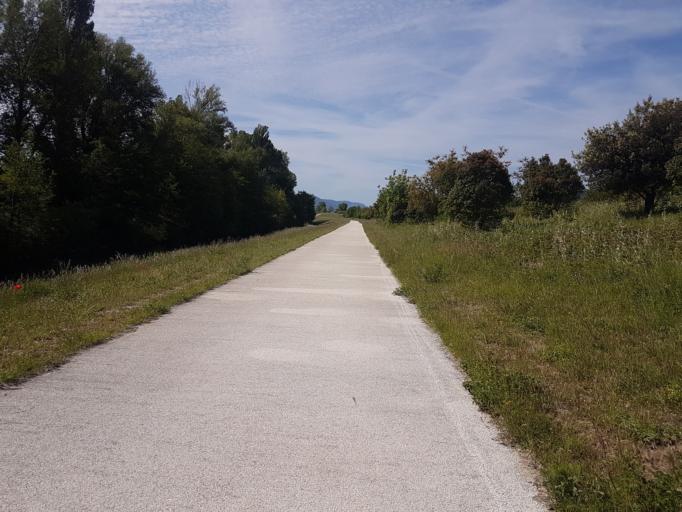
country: FR
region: Rhone-Alpes
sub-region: Departement de l'Ardeche
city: Le Pouzin
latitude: 44.7613
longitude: 4.7567
